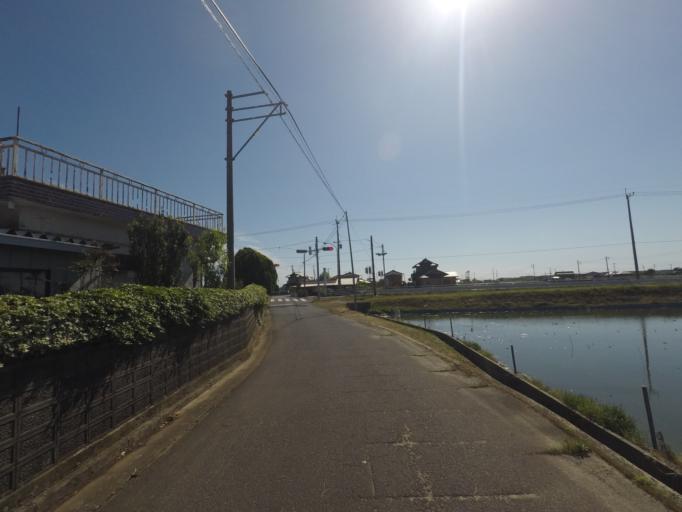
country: JP
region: Ibaraki
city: Inashiki
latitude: 36.0750
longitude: 140.4226
